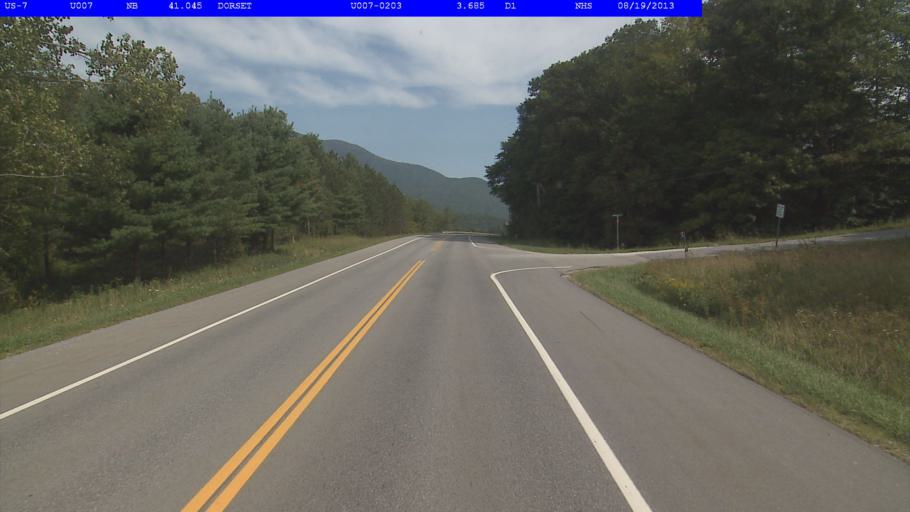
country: US
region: Vermont
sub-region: Bennington County
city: Manchester Center
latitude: 43.2624
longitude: -73.0079
